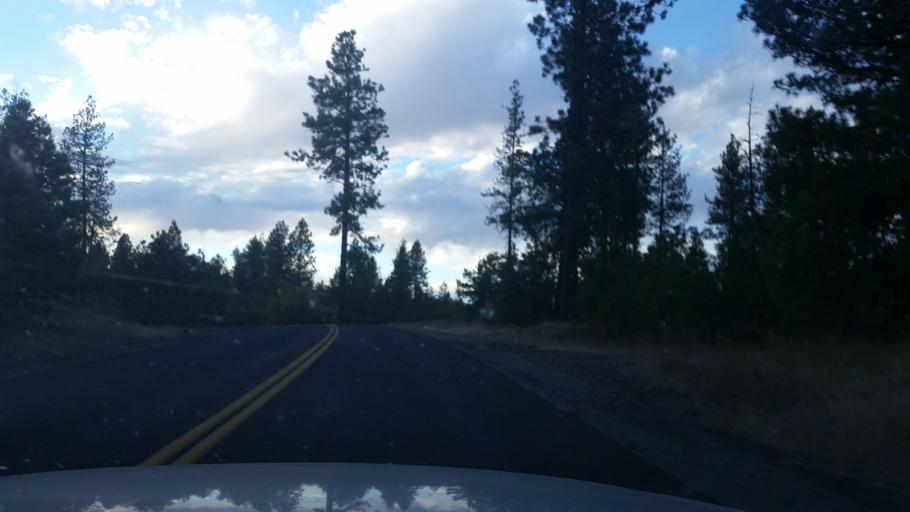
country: US
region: Washington
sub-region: Spokane County
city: Medical Lake
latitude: 47.5428
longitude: -117.6898
